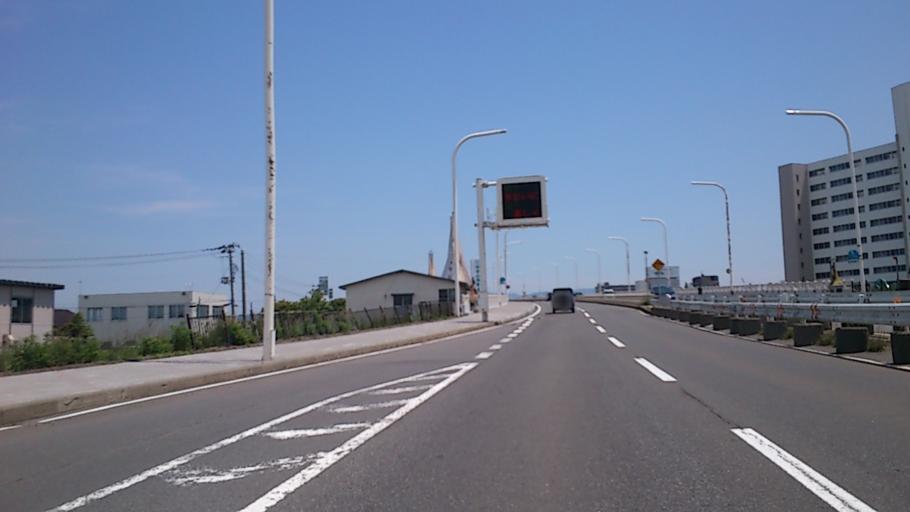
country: JP
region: Aomori
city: Aomori Shi
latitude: 40.8329
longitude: 140.7296
